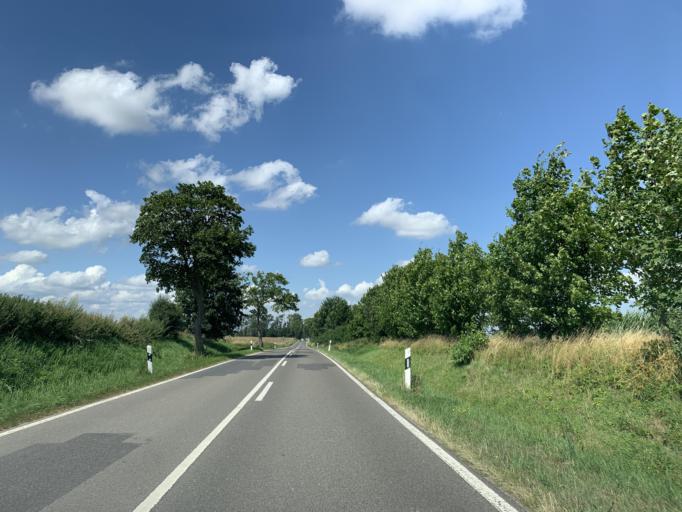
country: DE
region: Mecklenburg-Vorpommern
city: Blankensee
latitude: 53.3889
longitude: 13.3269
